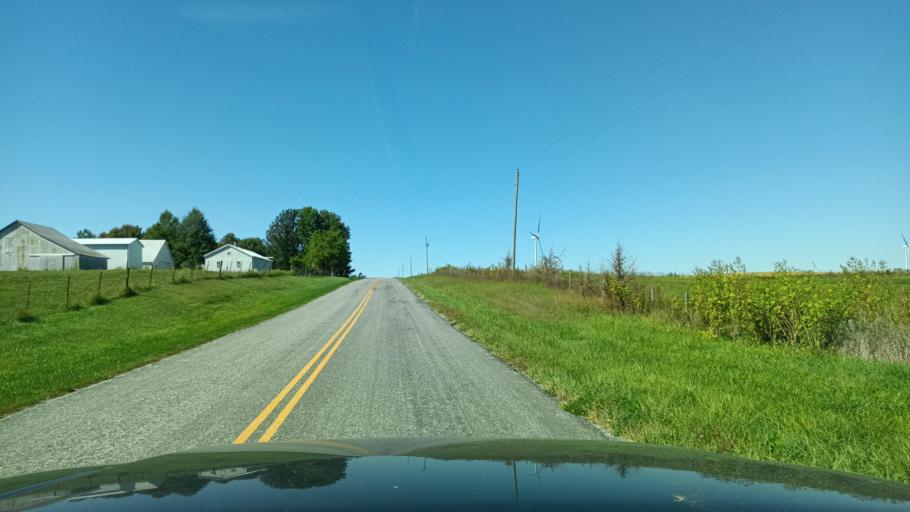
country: US
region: Missouri
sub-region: Adair County
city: Kirksville
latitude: 40.3307
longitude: -92.4682
